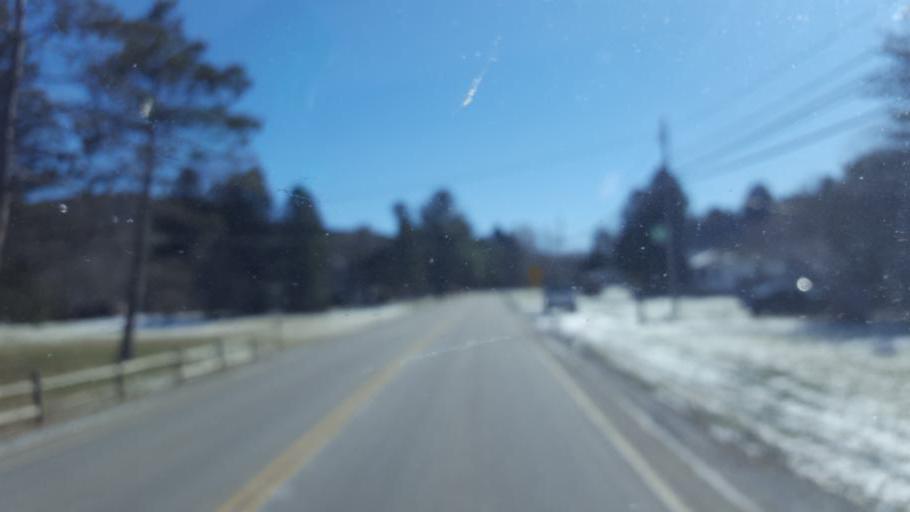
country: US
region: New York
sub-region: Allegany County
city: Wellsville
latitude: 42.0852
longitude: -77.9127
